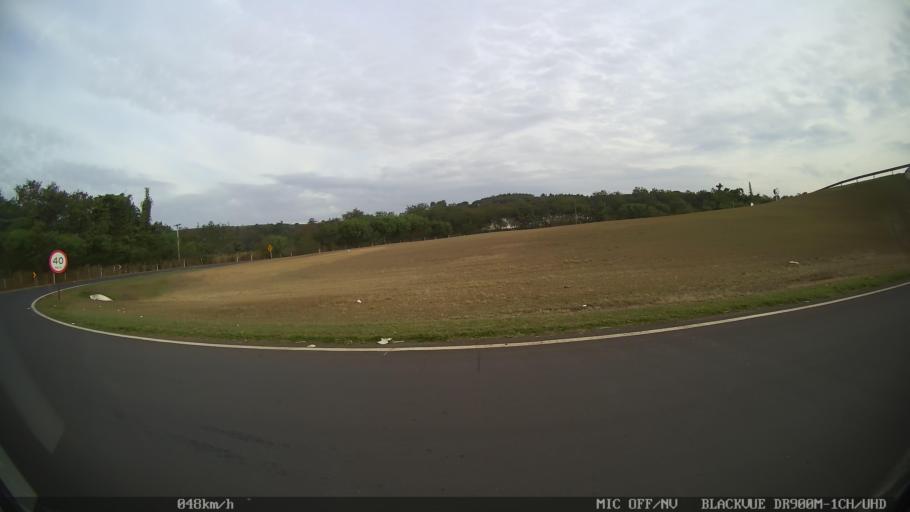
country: BR
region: Sao Paulo
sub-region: Piracicaba
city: Piracicaba
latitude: -22.6999
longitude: -47.6026
